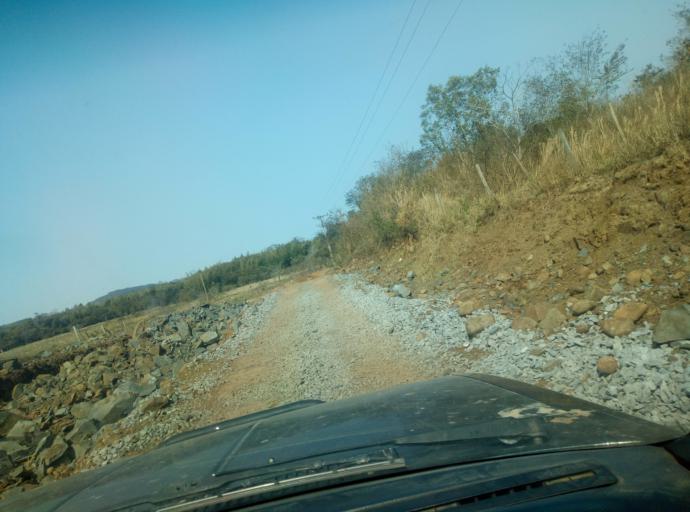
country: PY
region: Caaguazu
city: Coronel Oviedo
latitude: -25.3365
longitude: -56.3149
